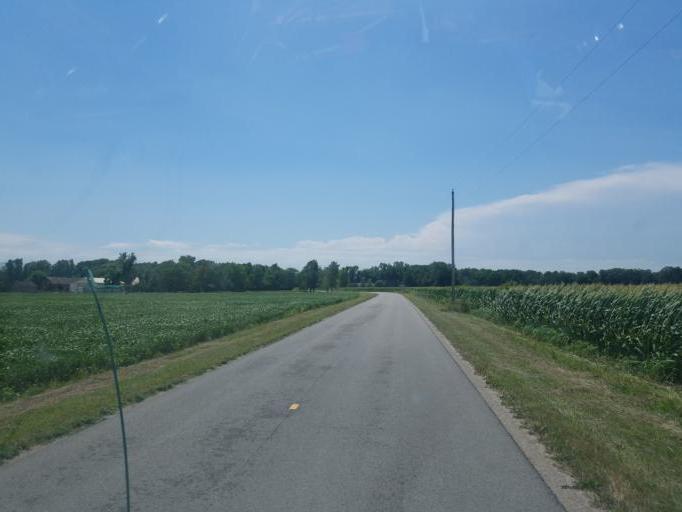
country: US
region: Ohio
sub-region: Paulding County
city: Antwerp
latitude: 41.1856
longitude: -84.7811
